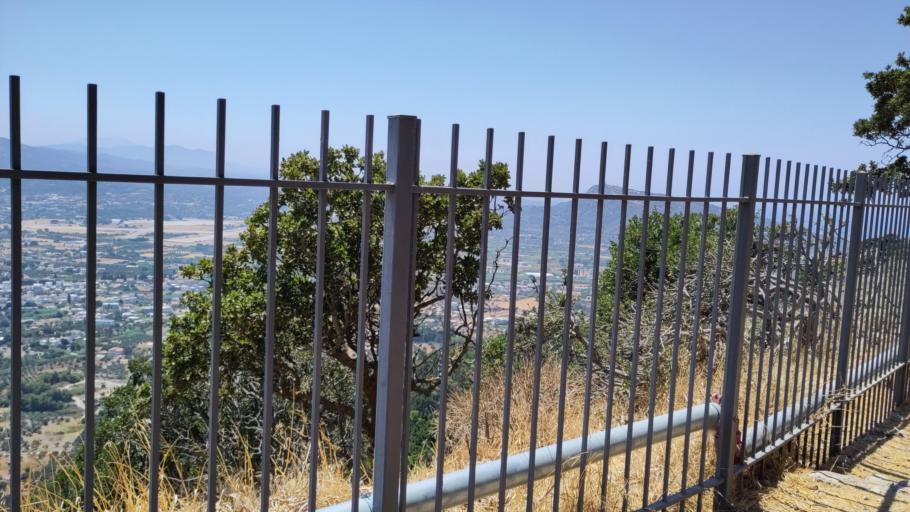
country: GR
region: South Aegean
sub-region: Nomos Dodekanisou
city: Trianta
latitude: 36.3981
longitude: 28.1443
